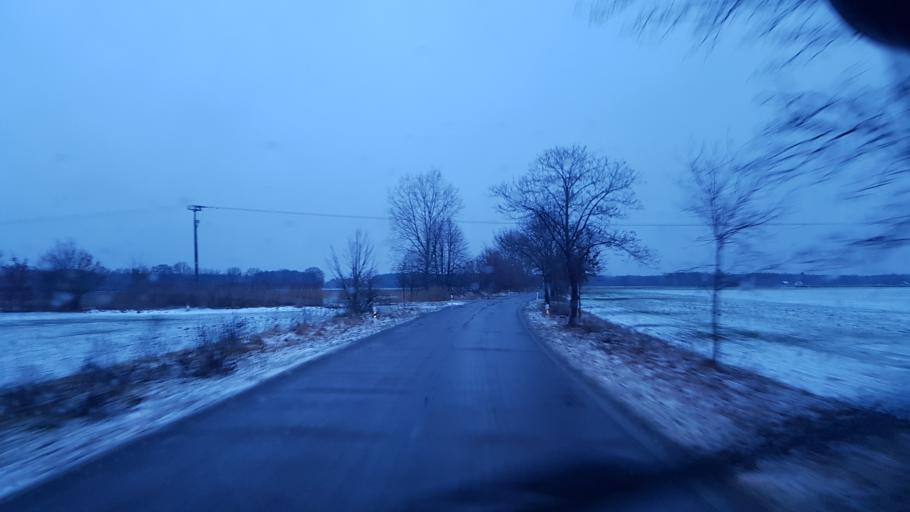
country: DE
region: Brandenburg
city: Drehnow
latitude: 51.8252
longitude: 14.3757
